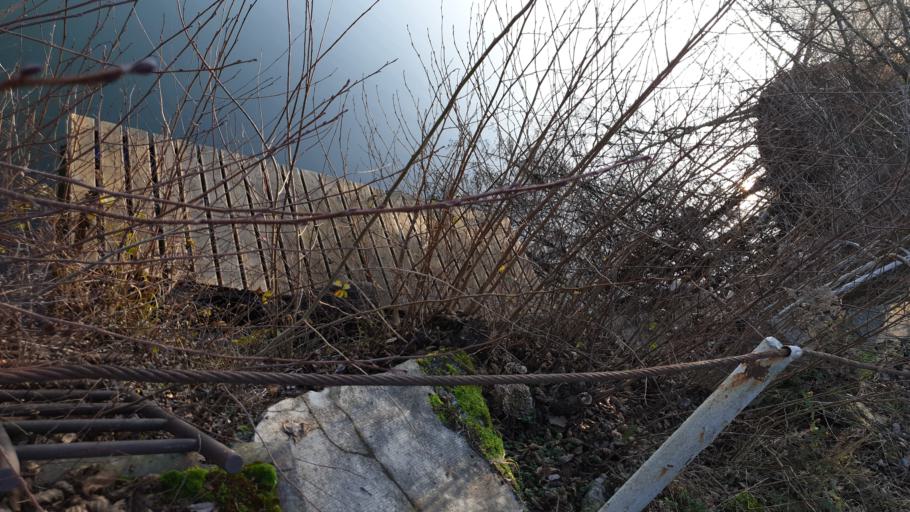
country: DE
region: Saxony
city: Hohburg
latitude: 51.4104
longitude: 12.7872
